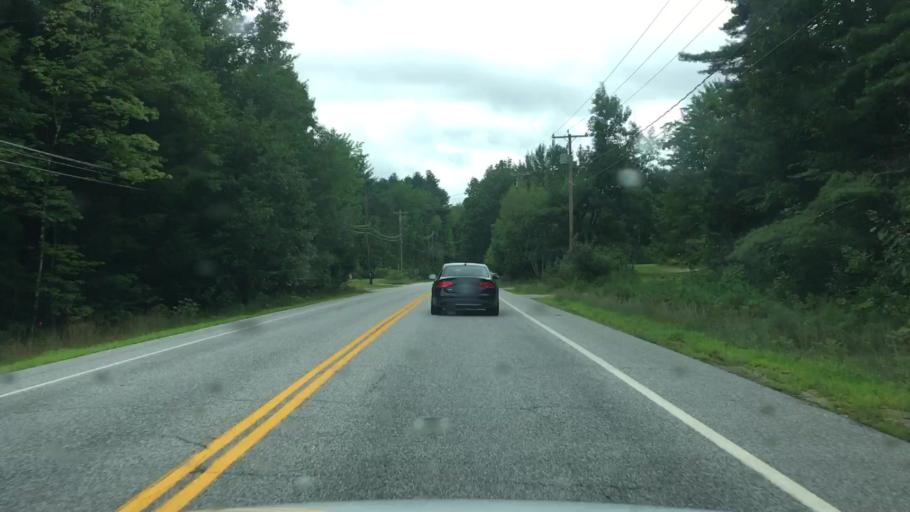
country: US
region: Maine
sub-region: York County
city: Cornish
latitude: 43.8374
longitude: -70.7796
